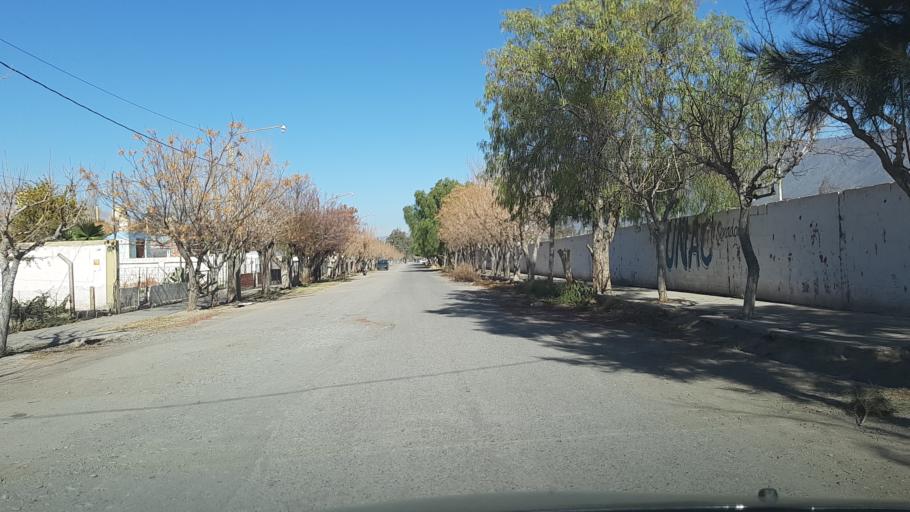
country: AR
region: San Juan
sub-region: Departamento de Zonda
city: Zonda
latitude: -31.5461
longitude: -68.7268
